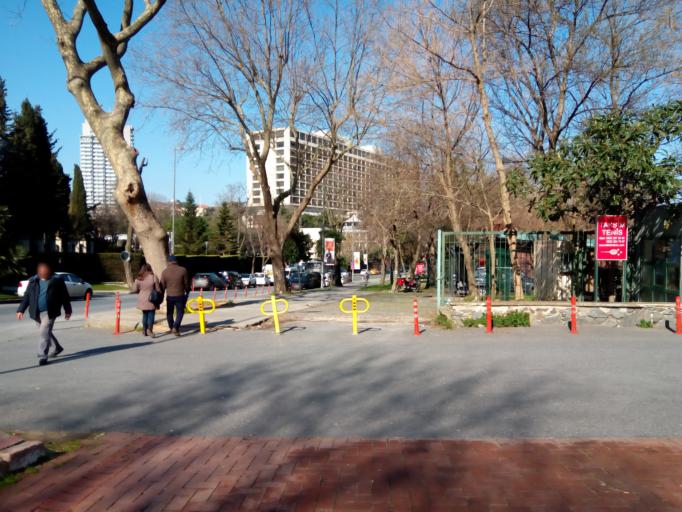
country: TR
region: Istanbul
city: Sisli
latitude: 41.0419
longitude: 28.9893
